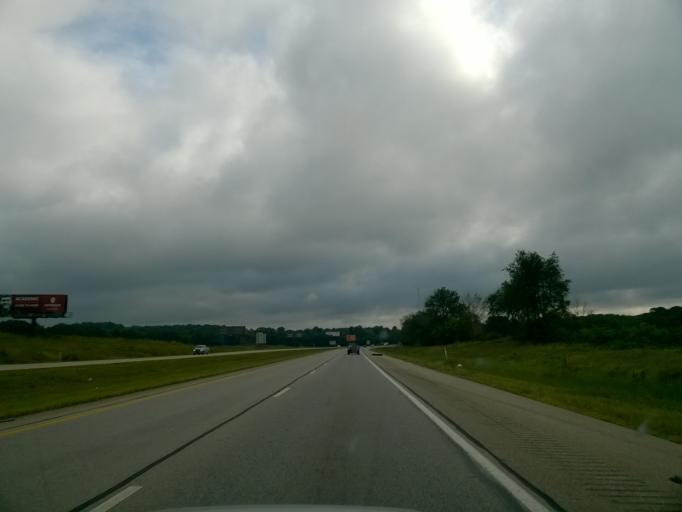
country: US
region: Indiana
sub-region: Harrison County
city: Corydon
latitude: 38.2420
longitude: -86.1091
